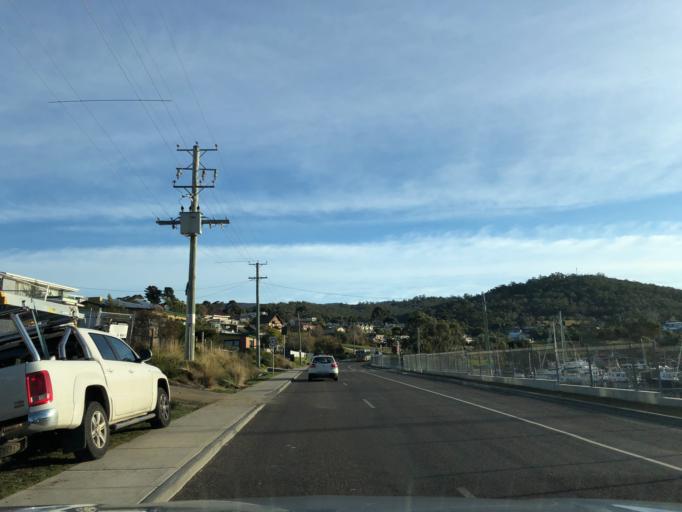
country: AU
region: Tasmania
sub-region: Kingborough
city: Kettering
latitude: -43.1278
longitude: 147.2530
